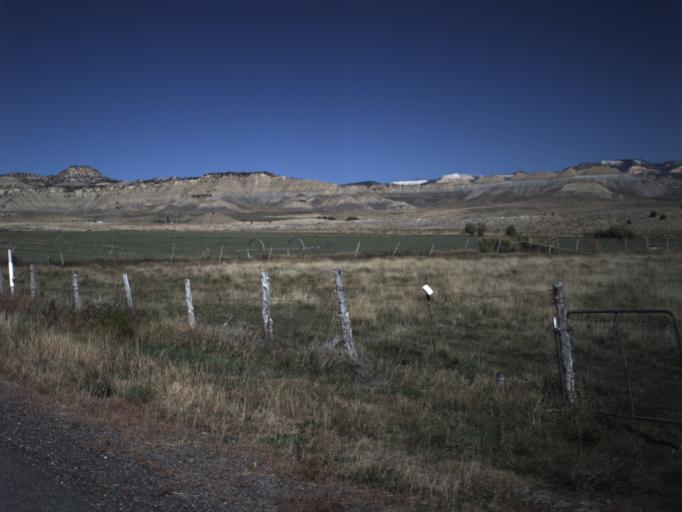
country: US
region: Utah
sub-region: Garfield County
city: Panguitch
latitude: 37.6319
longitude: -112.0818
